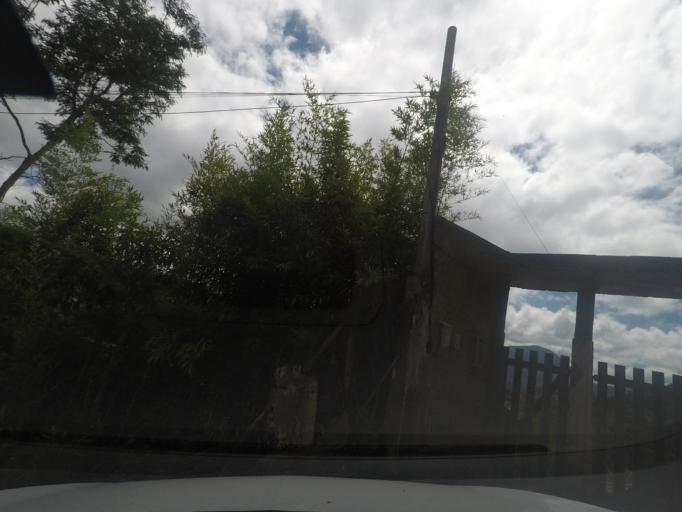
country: BR
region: Rio de Janeiro
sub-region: Teresopolis
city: Teresopolis
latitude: -22.4000
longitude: -42.9857
